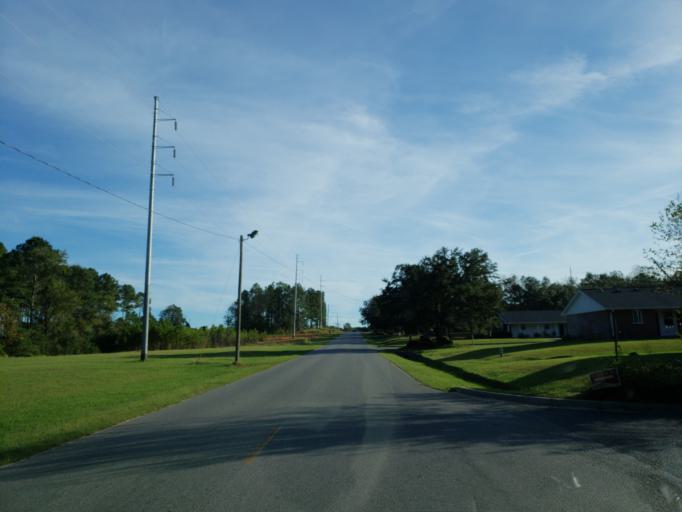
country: US
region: Georgia
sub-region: Dooly County
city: Vienna
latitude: 32.0852
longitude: -83.7878
